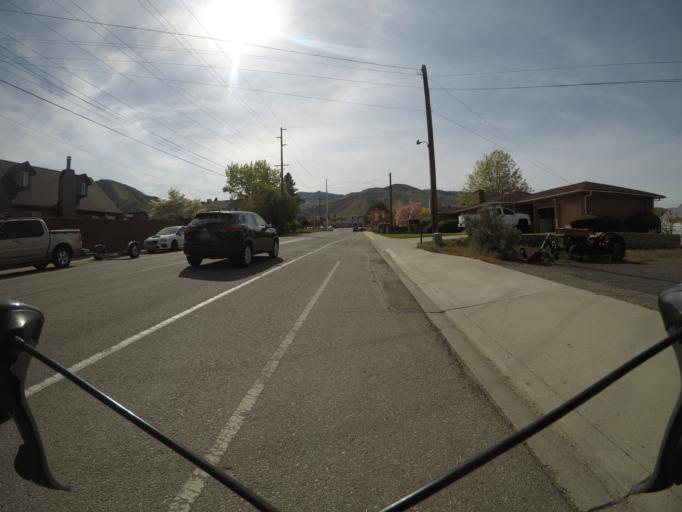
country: US
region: Washington
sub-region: Chelan County
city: West Wenatchee
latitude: 47.4328
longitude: -120.3446
